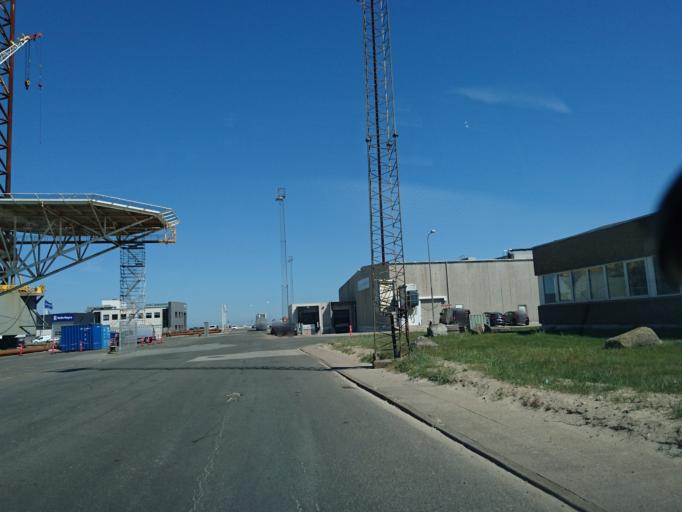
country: DK
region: North Denmark
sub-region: Hjorring Kommune
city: Hirtshals
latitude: 57.5912
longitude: 9.9827
